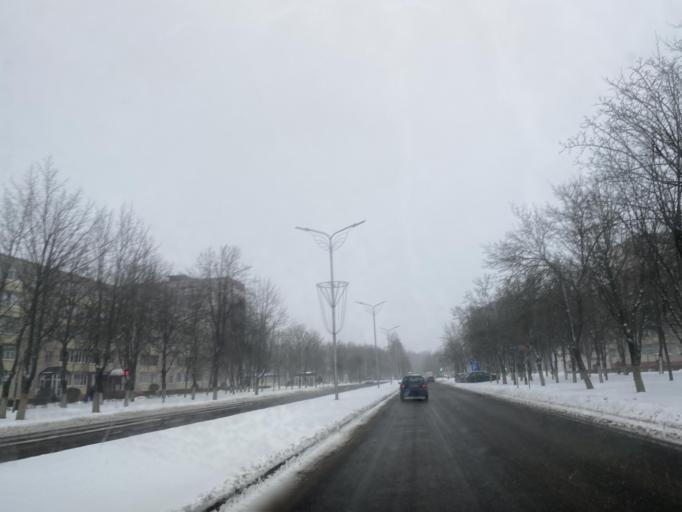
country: BY
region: Minsk
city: Horad Zhodzina
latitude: 54.0929
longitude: 28.3089
